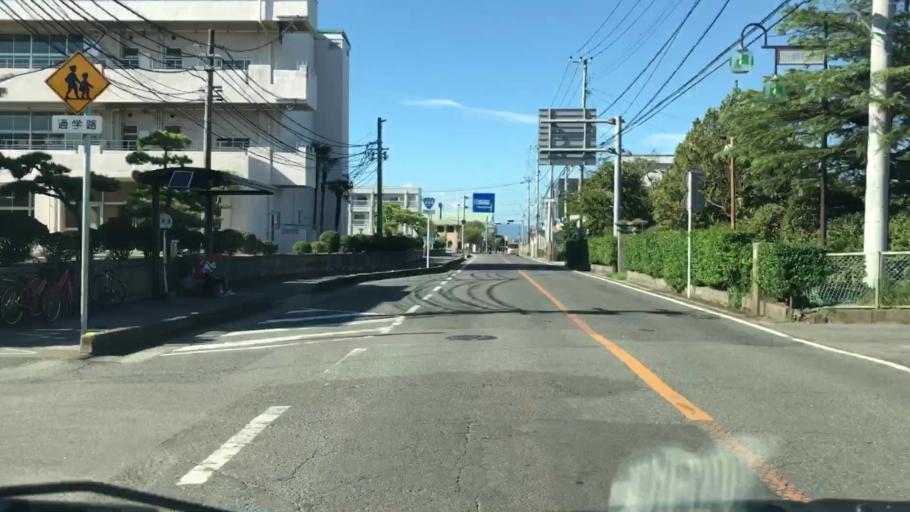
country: JP
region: Saga Prefecture
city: Okawa
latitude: 33.1900
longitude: 130.3195
